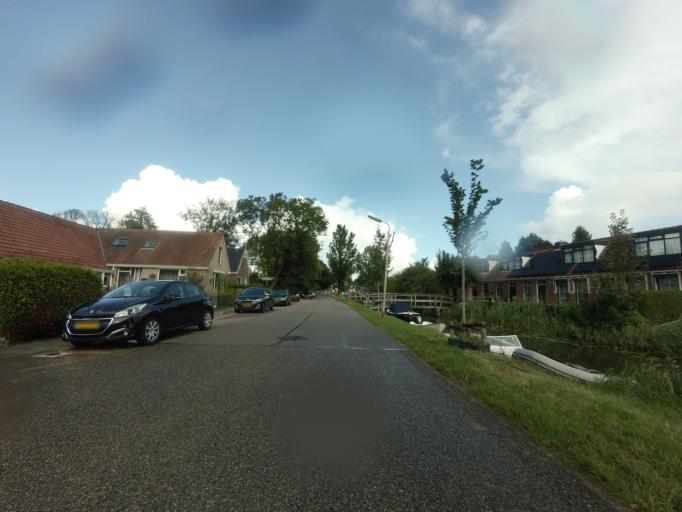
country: NL
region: Friesland
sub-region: Gemeente Leeuwarden
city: Wirdum
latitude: 53.1485
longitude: 5.8020
